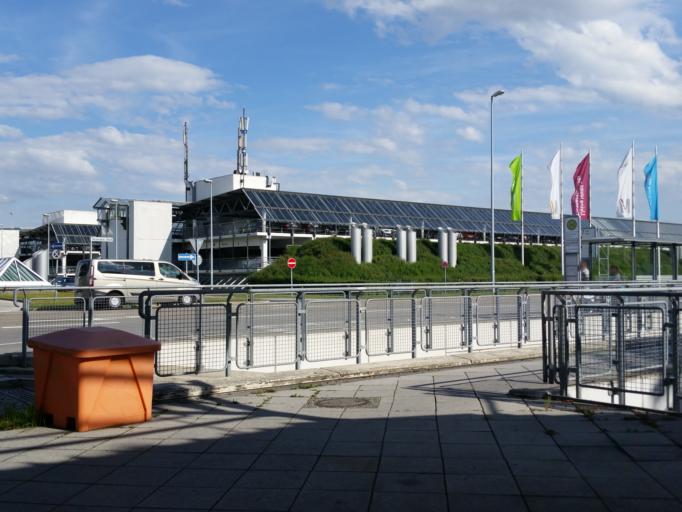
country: DE
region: Bavaria
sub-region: Upper Bavaria
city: Hallbergmoos
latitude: 48.3510
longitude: 11.7854
